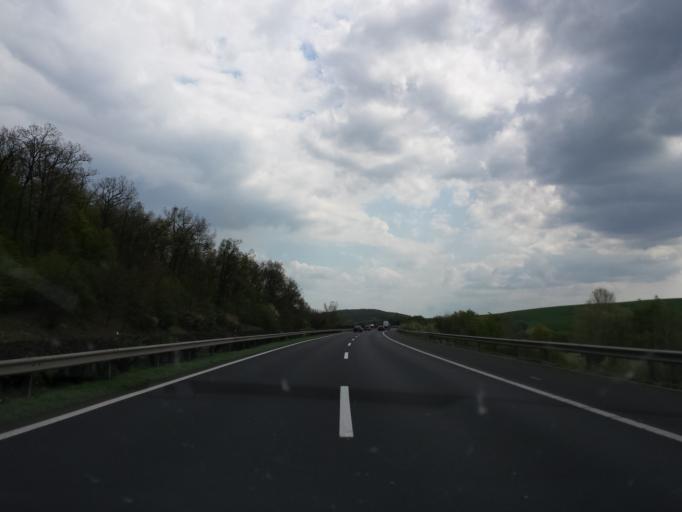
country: HU
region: Komarom-Esztergom
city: Tarjan
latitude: 47.5687
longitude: 18.4769
